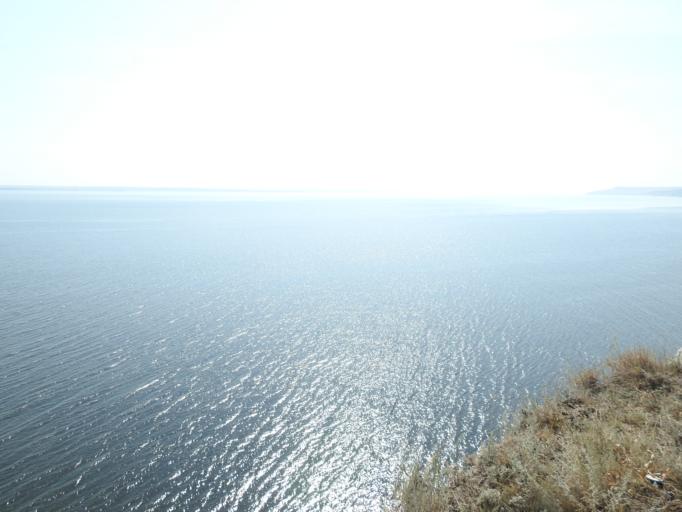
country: RU
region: Saratov
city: Kamenskiy
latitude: 50.6486
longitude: 45.6472
